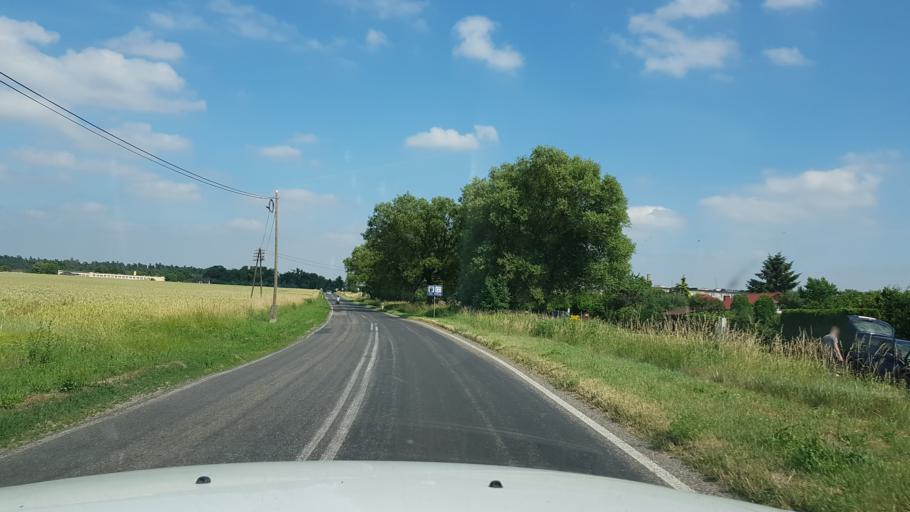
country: PL
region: West Pomeranian Voivodeship
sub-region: Powiat goleniowski
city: Mosty
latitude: 53.5481
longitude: 14.9439
